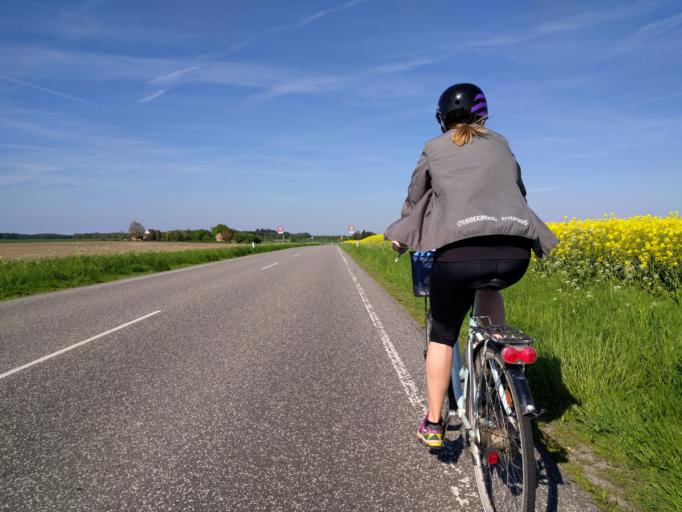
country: DK
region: Zealand
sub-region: Guldborgsund Kommune
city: Nykobing Falster
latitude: 54.7590
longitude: 11.9296
